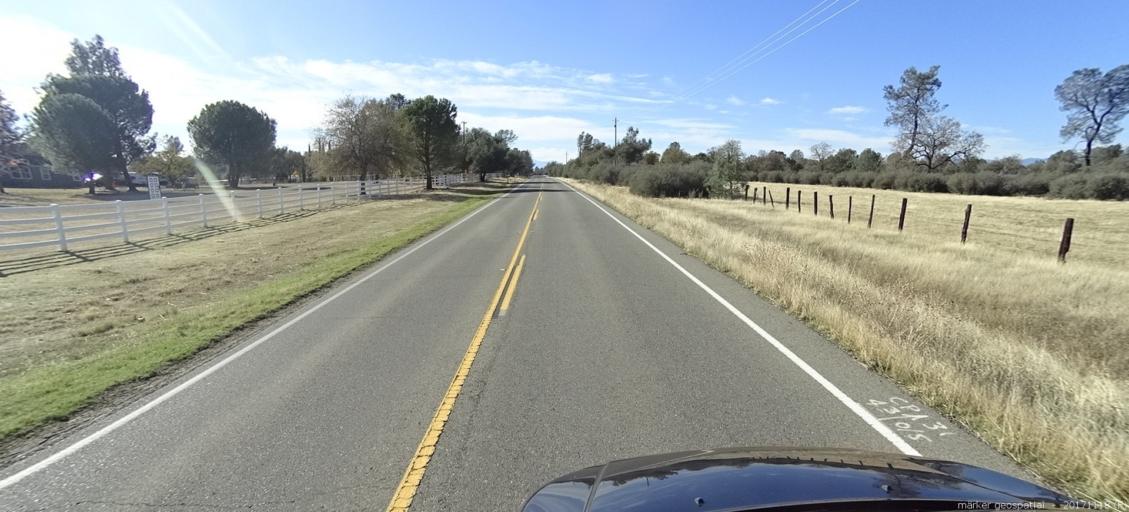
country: US
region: California
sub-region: Shasta County
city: Anderson
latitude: 40.4423
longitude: -122.3770
